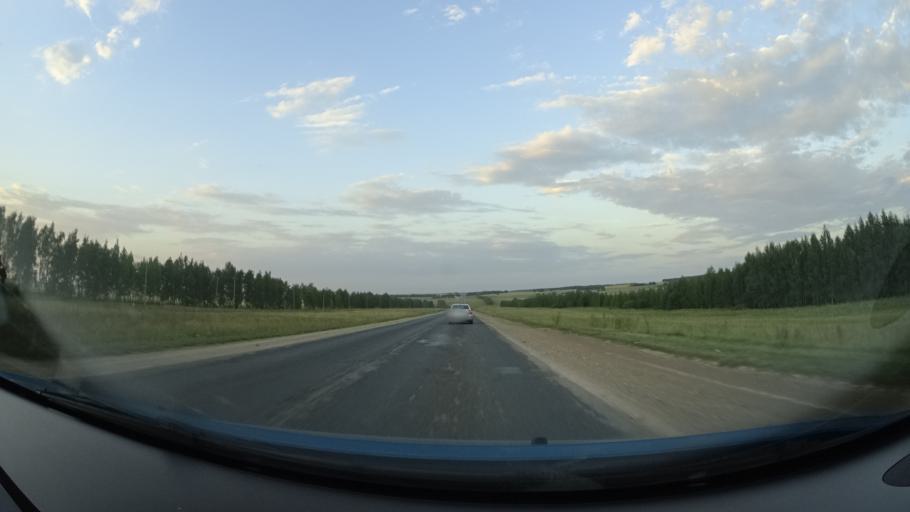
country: RU
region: Orenburg
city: Severnoye
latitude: 54.2287
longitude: 52.7603
